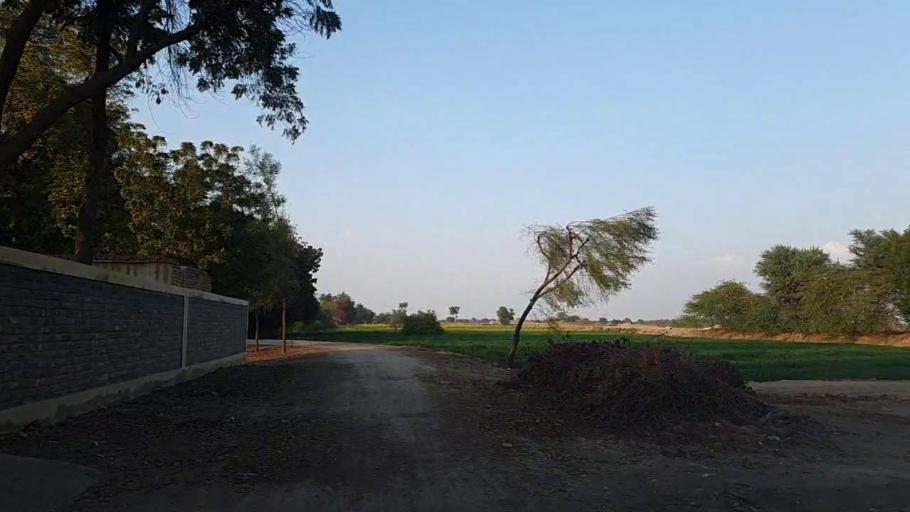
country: PK
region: Sindh
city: Jam Sahib
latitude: 26.3738
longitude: 68.5871
